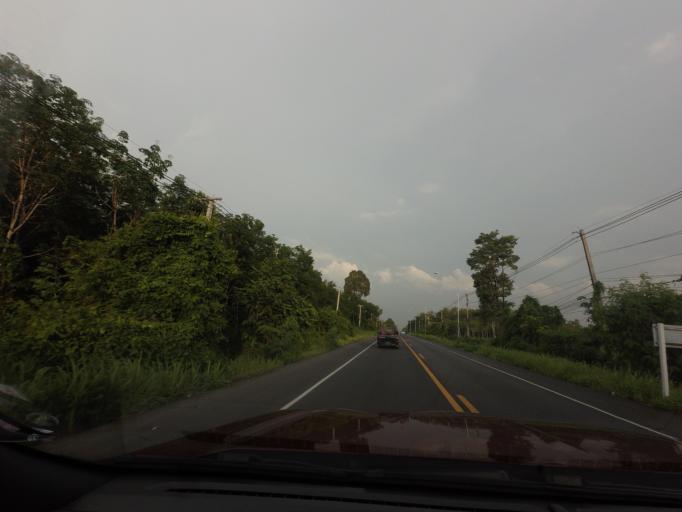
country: TH
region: Pattani
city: Mae Lan
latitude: 6.6586
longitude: 101.1702
